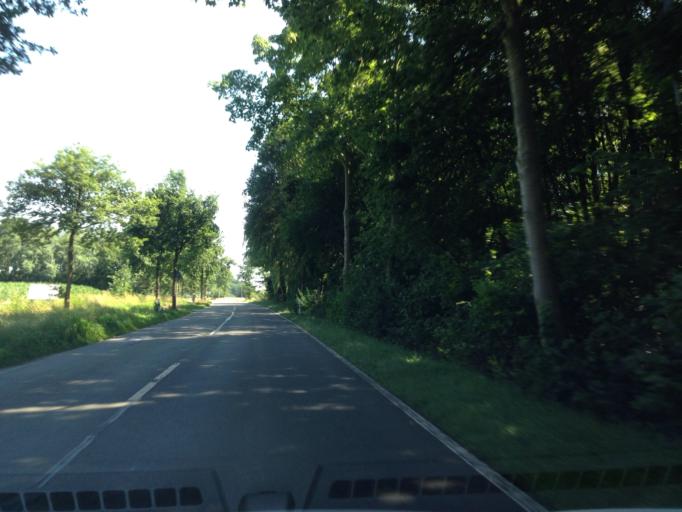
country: DE
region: North Rhine-Westphalia
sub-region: Regierungsbezirk Munster
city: Altenberge
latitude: 51.9942
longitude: 7.5288
